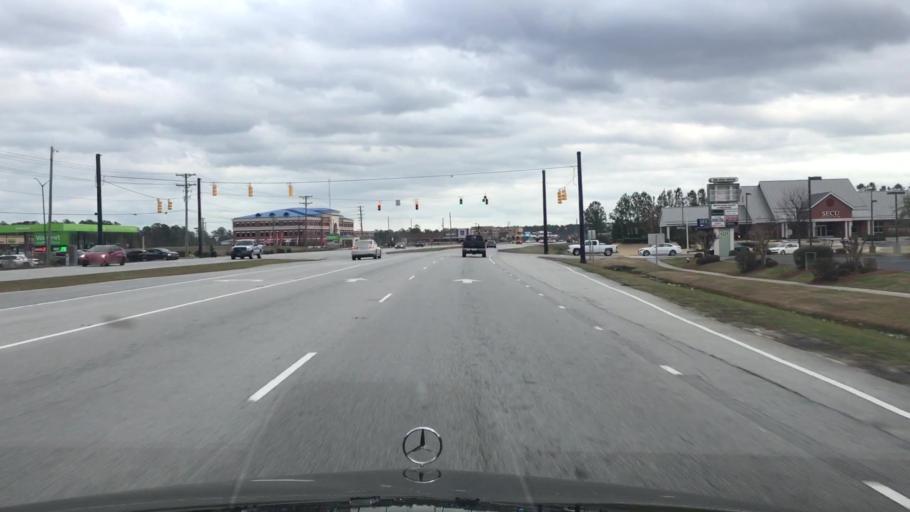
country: US
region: North Carolina
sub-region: Onslow County
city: Pumpkin Center
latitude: 34.8003
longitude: -77.4184
